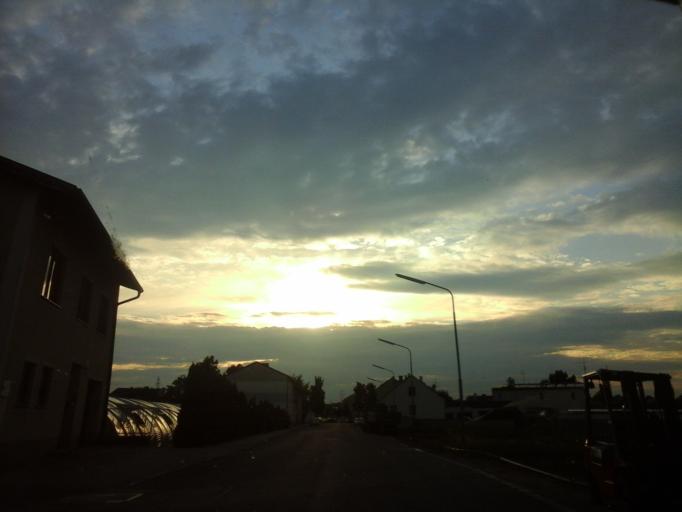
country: AT
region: Lower Austria
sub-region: Politischer Bezirk Wien-Umgebung
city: Schwechat
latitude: 48.1594
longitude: 16.4875
